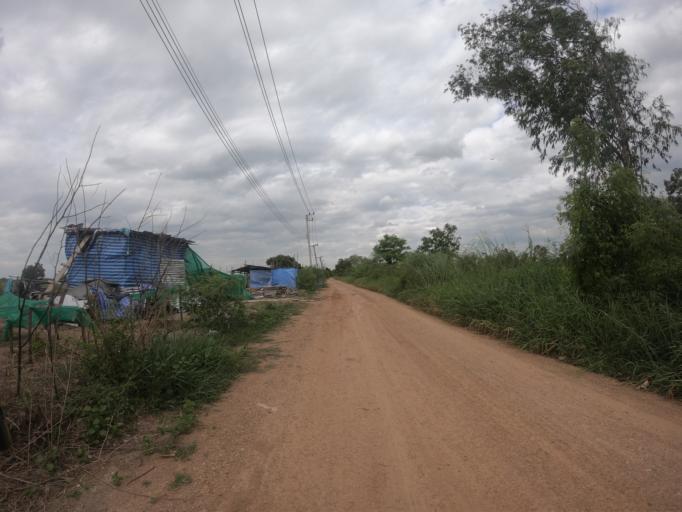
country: TH
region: Pathum Thani
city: Nong Suea
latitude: 14.0762
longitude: 100.8389
